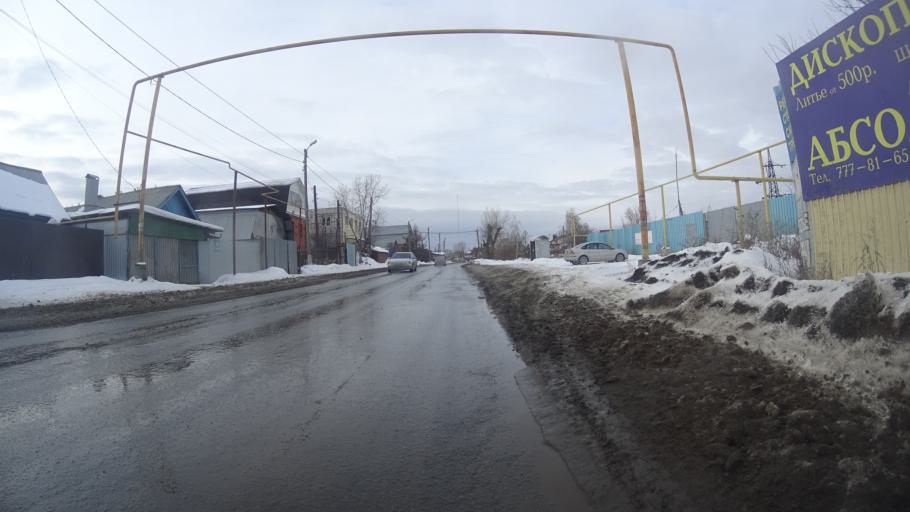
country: RU
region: Chelyabinsk
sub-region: Gorod Chelyabinsk
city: Chelyabinsk
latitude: 55.1294
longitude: 61.3995
